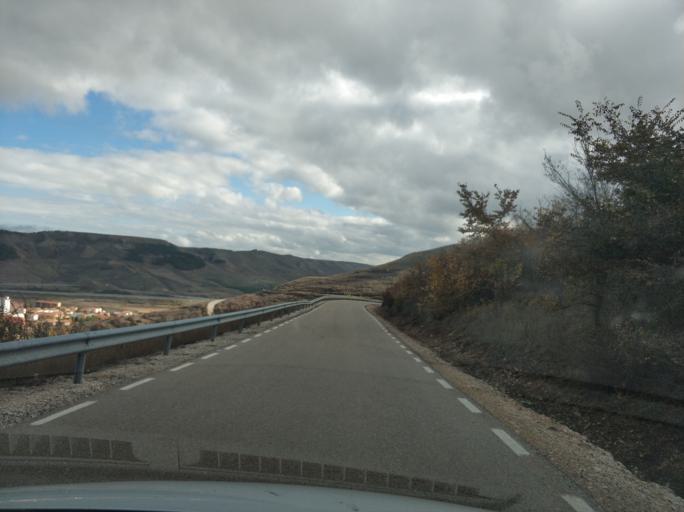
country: ES
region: Castille and Leon
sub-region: Provincia de Soria
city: Medinaceli
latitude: 41.1659
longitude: -2.4346
